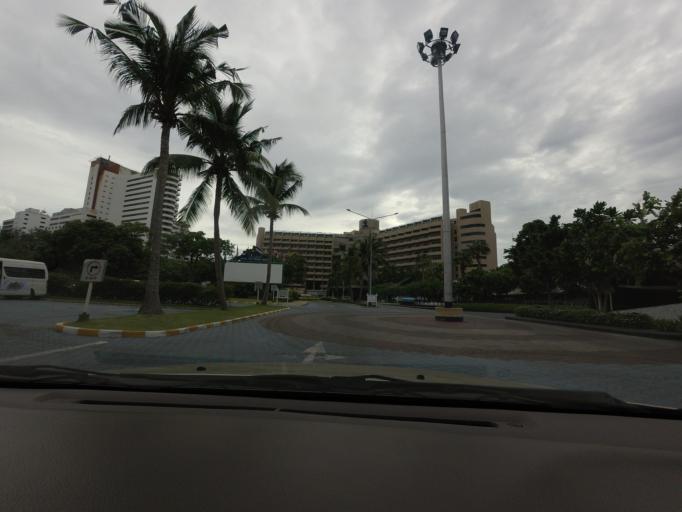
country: TH
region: Chon Buri
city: Phatthaya
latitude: 12.9237
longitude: 100.8613
